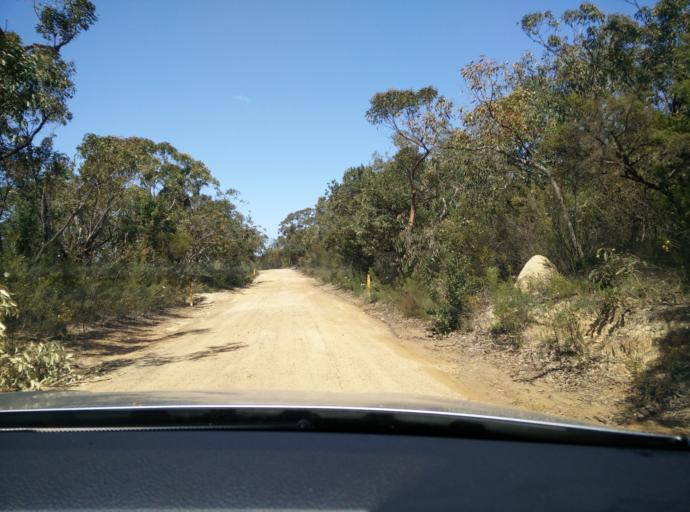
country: AU
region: New South Wales
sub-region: Gosford Shire
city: Umina
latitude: -33.5424
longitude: 151.2822
